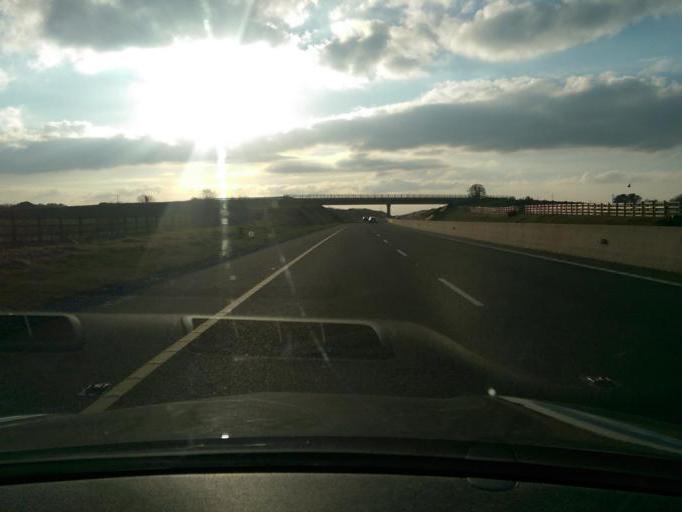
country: IE
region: Munster
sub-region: North Tipperary
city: Templemore
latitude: 52.8831
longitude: -7.9784
